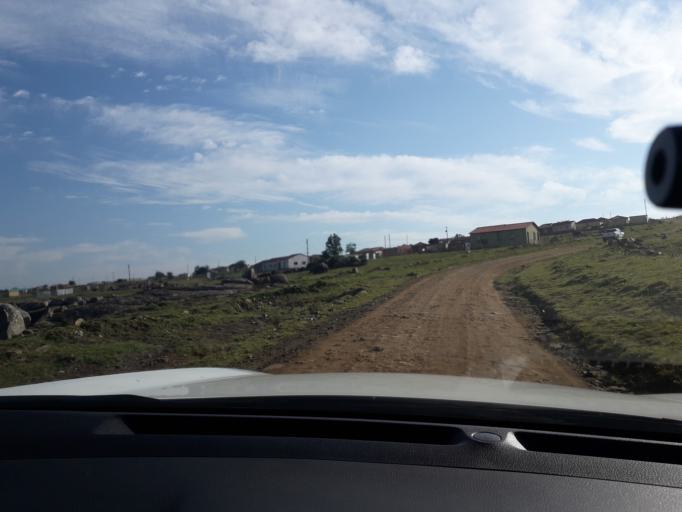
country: ZA
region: Eastern Cape
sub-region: Buffalo City Metropolitan Municipality
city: Bhisho
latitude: -32.9417
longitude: 27.2891
